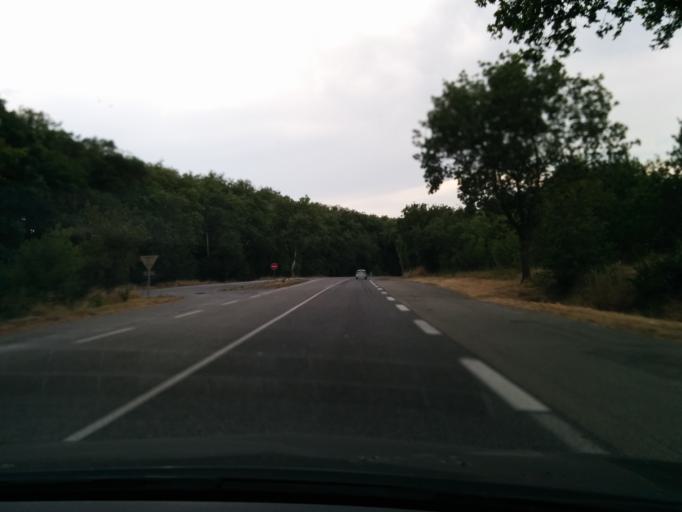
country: FR
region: Languedoc-Roussillon
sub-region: Departement de l'Aude
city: Saint-Martin-Lalande
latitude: 43.2989
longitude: 1.9907
